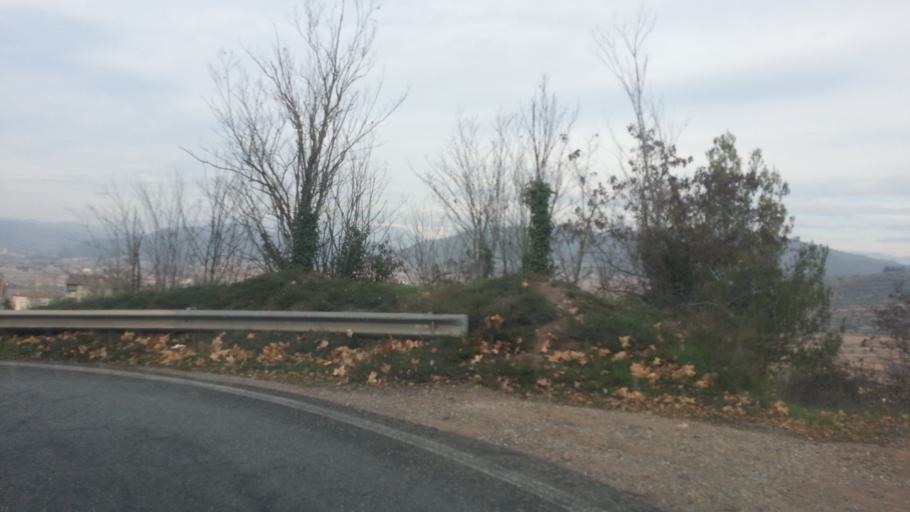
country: ES
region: Catalonia
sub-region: Provincia de Barcelona
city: Cardona
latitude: 41.9159
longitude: 1.6846
